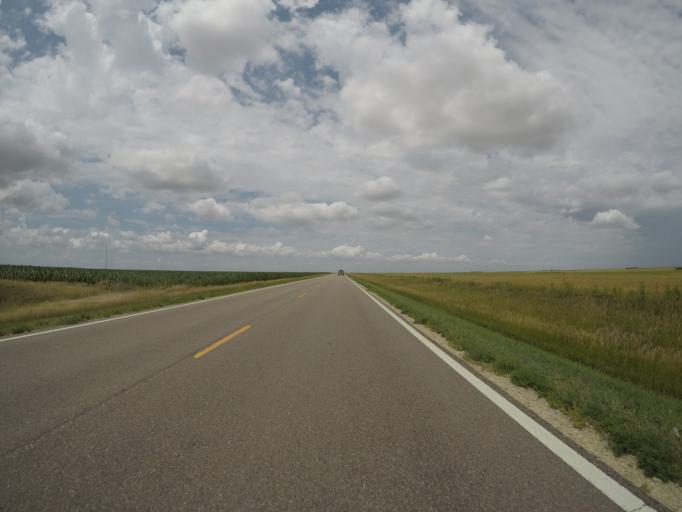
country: US
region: Kansas
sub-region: Rawlins County
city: Atwood
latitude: 39.7232
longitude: -101.0563
